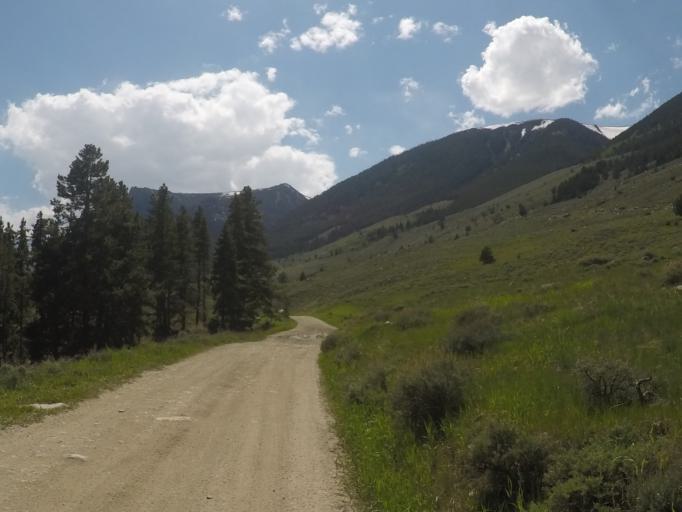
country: US
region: Montana
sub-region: Carbon County
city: Red Lodge
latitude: 45.0608
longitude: -109.4105
